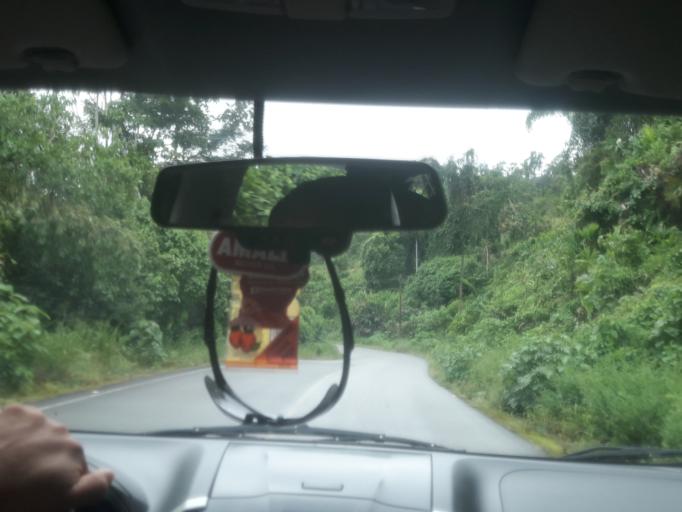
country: EC
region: Napo
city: Tena
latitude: -1.0354
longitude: -77.7176
